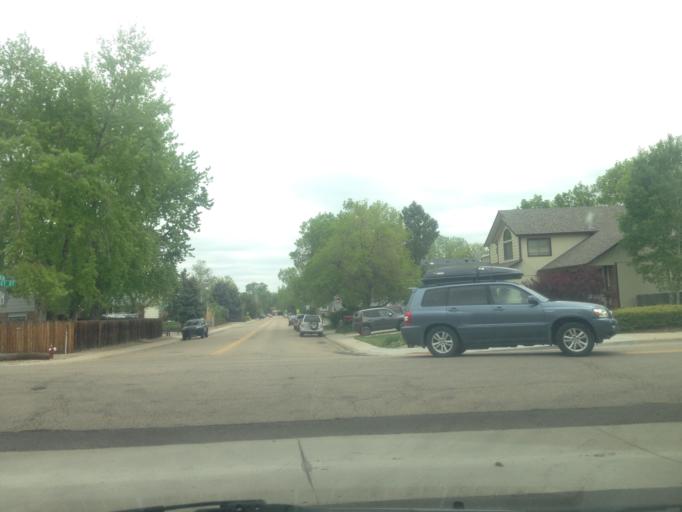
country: US
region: Colorado
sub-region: Boulder County
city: Longmont
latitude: 40.1398
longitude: -105.1218
